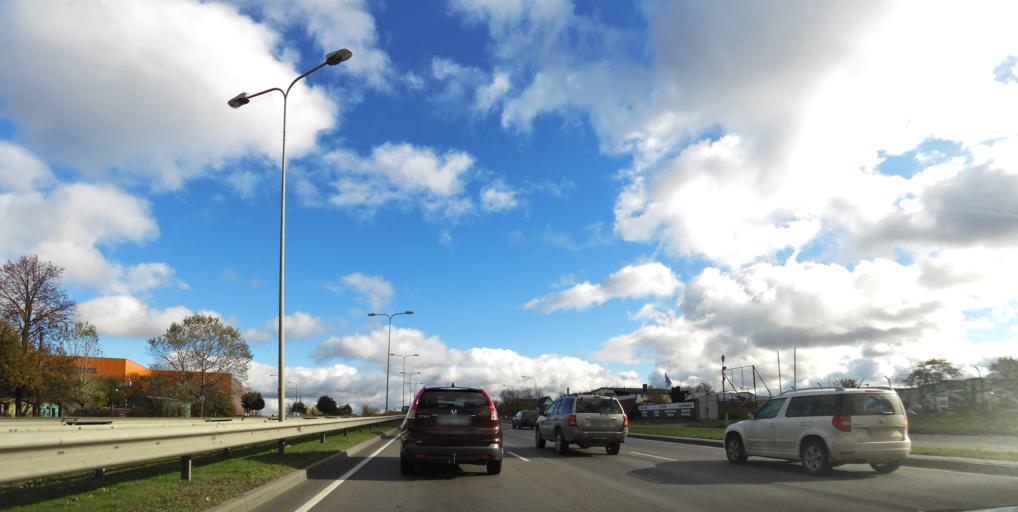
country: LT
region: Vilnius County
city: Rasos
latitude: 54.6548
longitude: 25.2990
